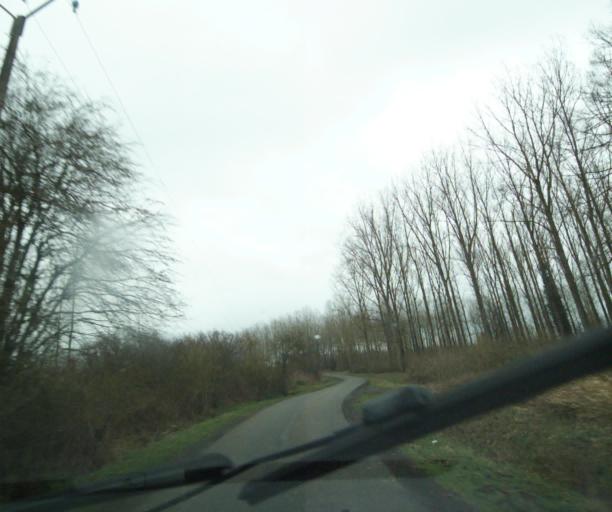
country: FR
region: Nord-Pas-de-Calais
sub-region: Departement du Nord
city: Vicq
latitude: 50.4210
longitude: 3.6301
